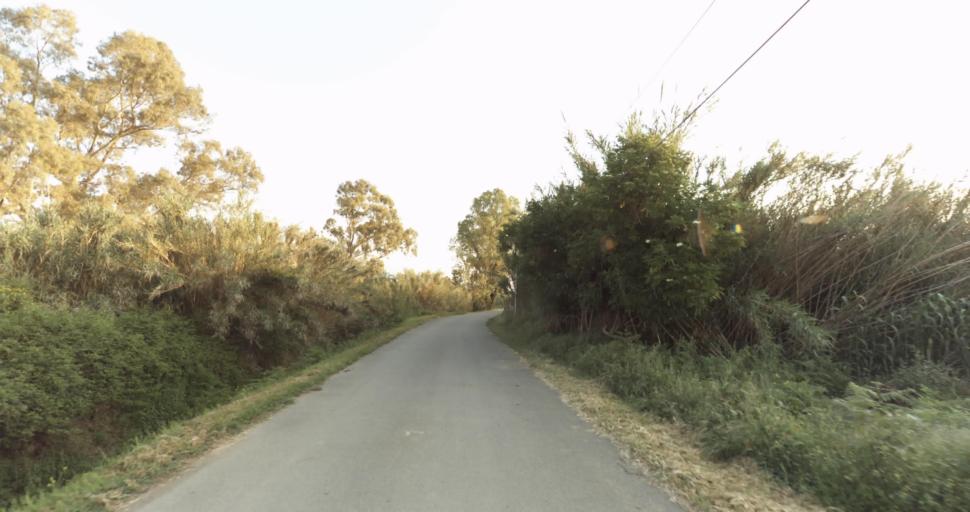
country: FR
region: Corsica
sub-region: Departement de la Haute-Corse
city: Biguglia
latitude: 42.6170
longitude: 9.4457
